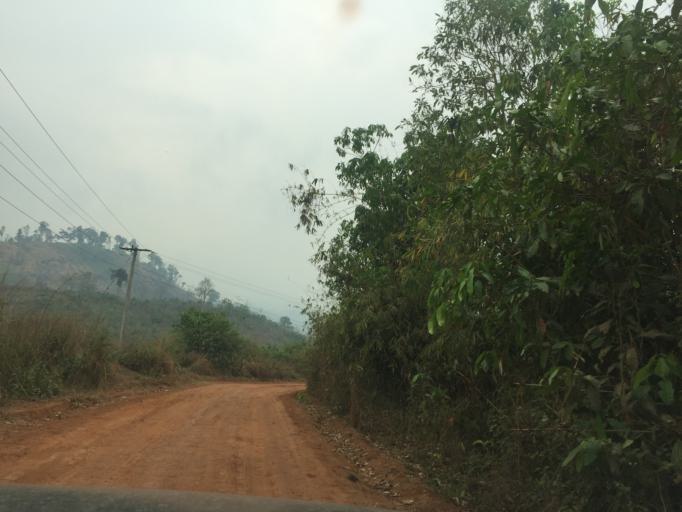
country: TH
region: Nan
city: Bo Kluea
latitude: 18.8547
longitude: 101.4234
